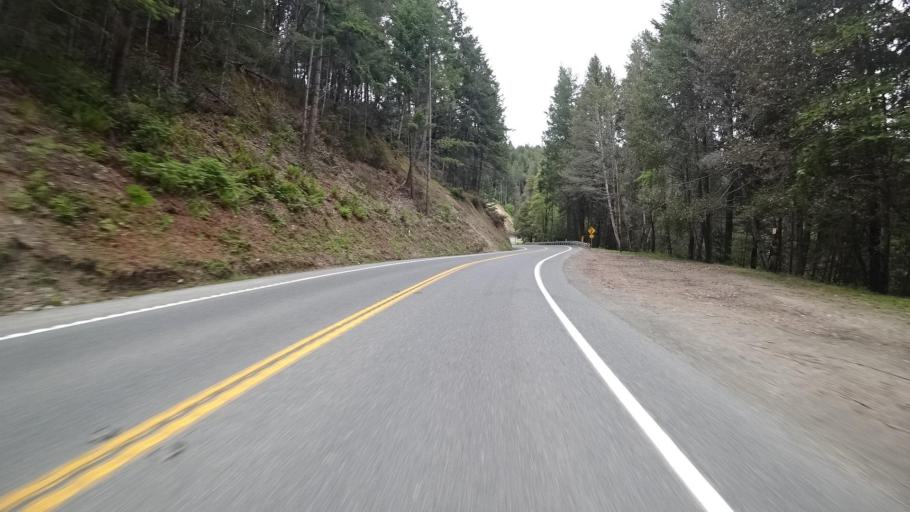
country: US
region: California
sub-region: Humboldt County
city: Willow Creek
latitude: 41.0022
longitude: -123.6484
